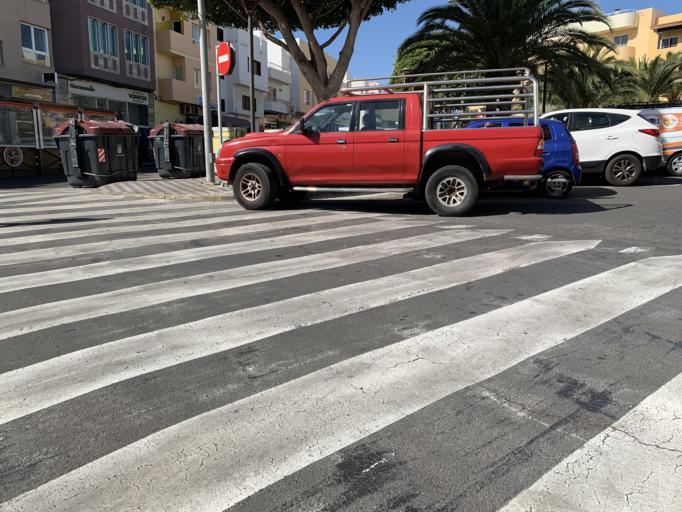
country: ES
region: Canary Islands
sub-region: Provincia de Las Palmas
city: Puerto del Rosario
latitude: 28.5021
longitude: -13.8703
